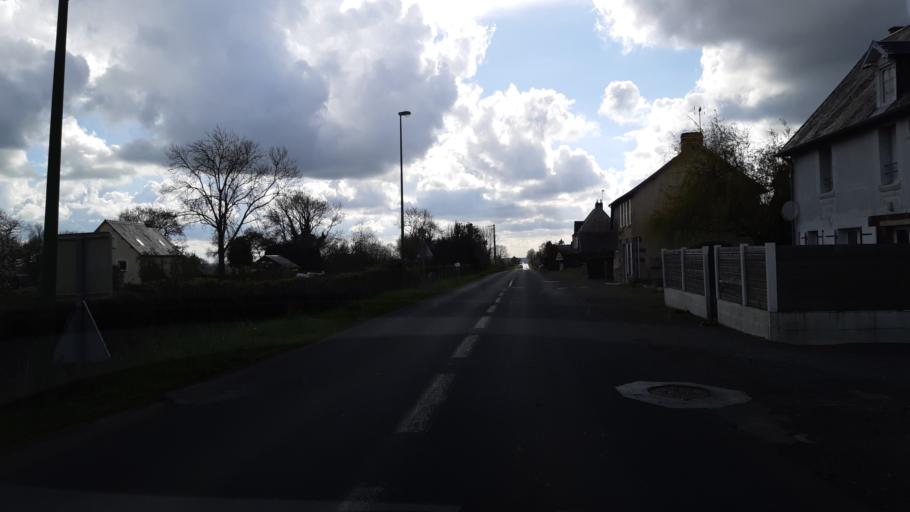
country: FR
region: Lower Normandy
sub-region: Departement de la Manche
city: Gavray
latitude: 48.9327
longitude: -1.3849
